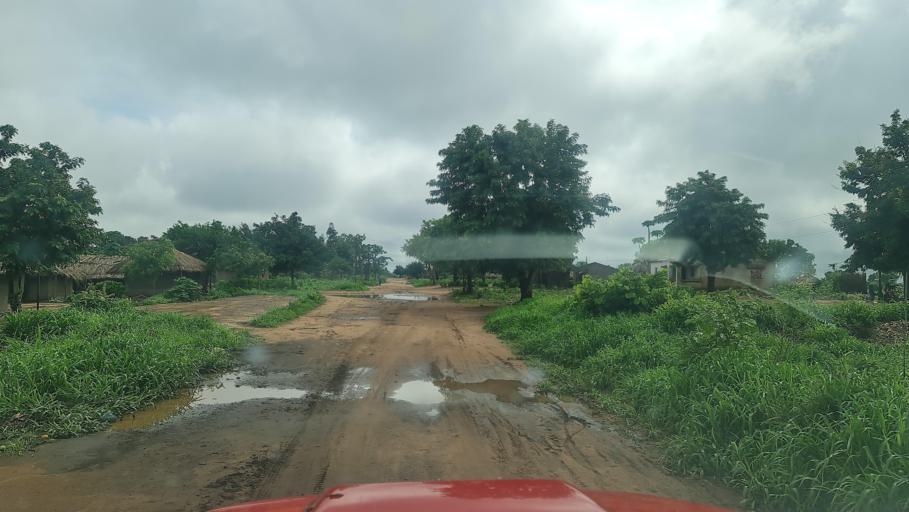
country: MW
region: Southern Region
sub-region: Nsanje District
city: Nsanje
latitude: -17.2215
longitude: 35.6695
